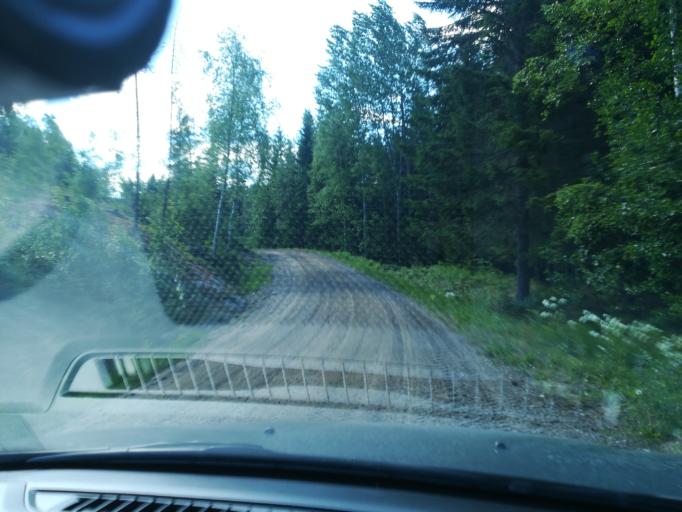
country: FI
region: Southern Savonia
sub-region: Mikkeli
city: Puumala
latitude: 61.6502
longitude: 28.1874
